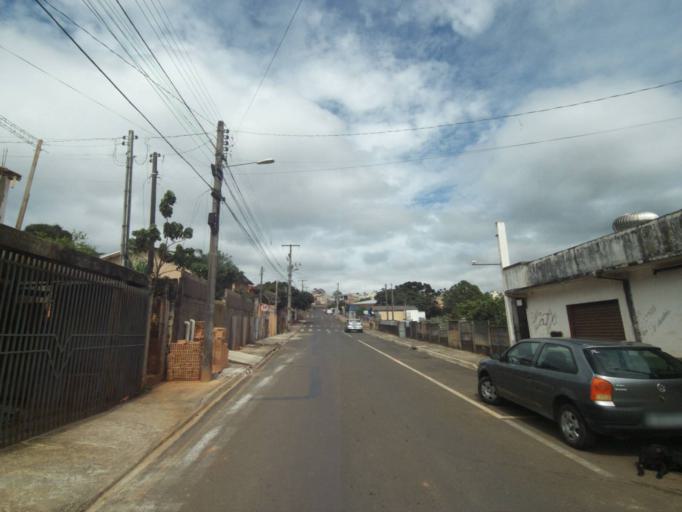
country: BR
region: Parana
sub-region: Telemaco Borba
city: Telemaco Borba
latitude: -24.3327
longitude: -50.6390
